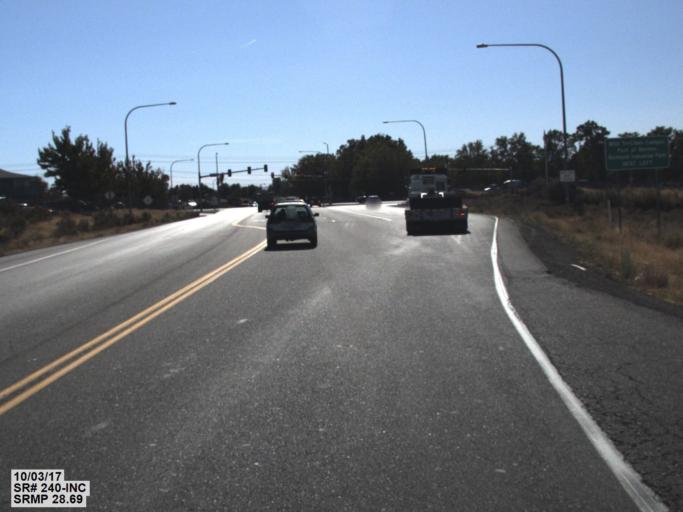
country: US
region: Washington
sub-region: Benton County
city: Richland
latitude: 46.3106
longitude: -119.2875
